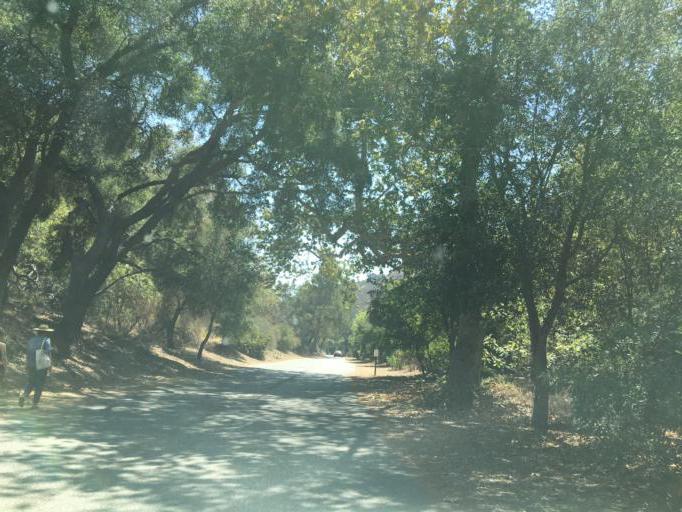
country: US
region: California
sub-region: Los Angeles County
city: Beverly Hills
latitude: 34.1097
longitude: -118.4154
